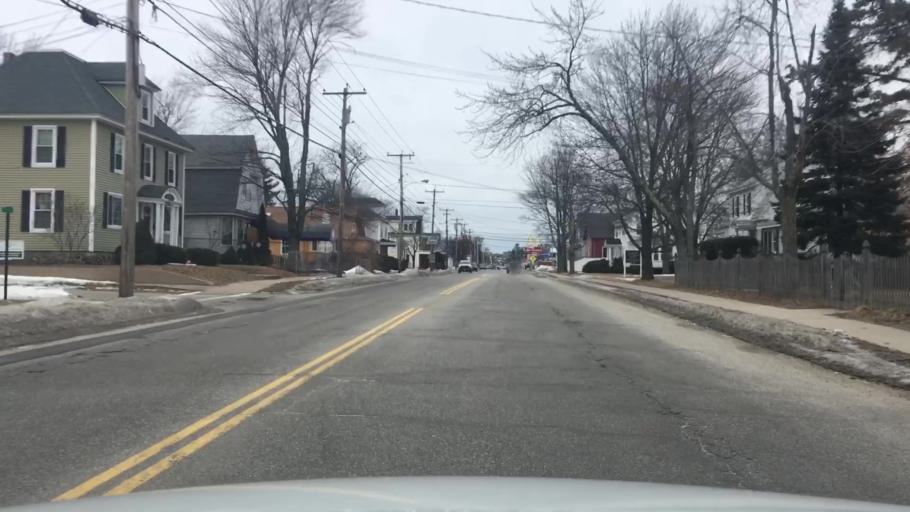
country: US
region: Maine
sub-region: York County
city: Sanford (historical)
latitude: 43.4304
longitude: -70.7690
